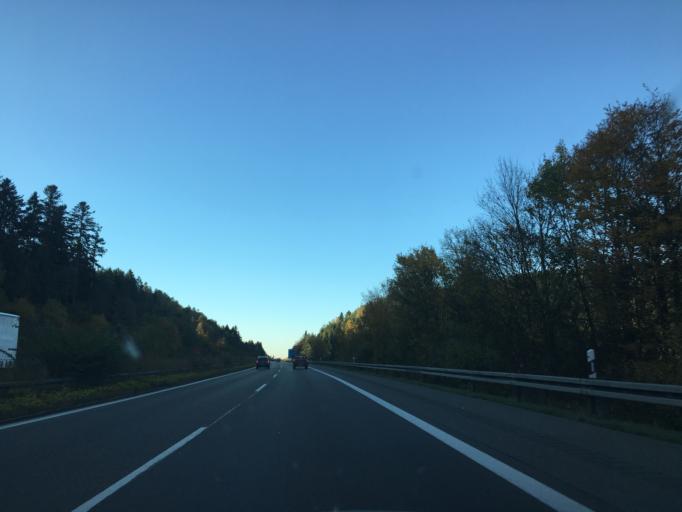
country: DE
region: Baden-Wuerttemberg
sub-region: Freiburg Region
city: Vohringen
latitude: 48.2866
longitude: 8.6401
